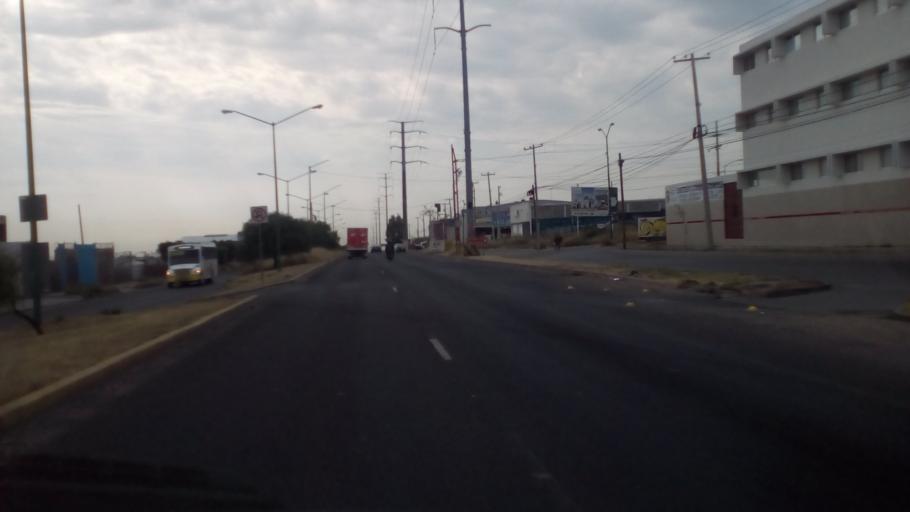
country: MX
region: Guanajuato
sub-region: Leon
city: La Ermita
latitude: 21.1604
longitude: -101.7328
